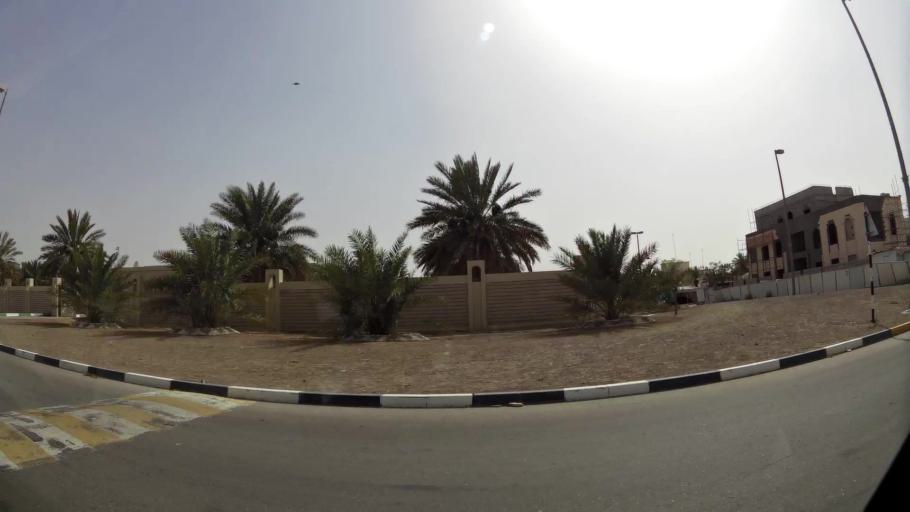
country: AE
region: Abu Dhabi
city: Al Ain
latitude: 24.1810
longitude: 55.6198
